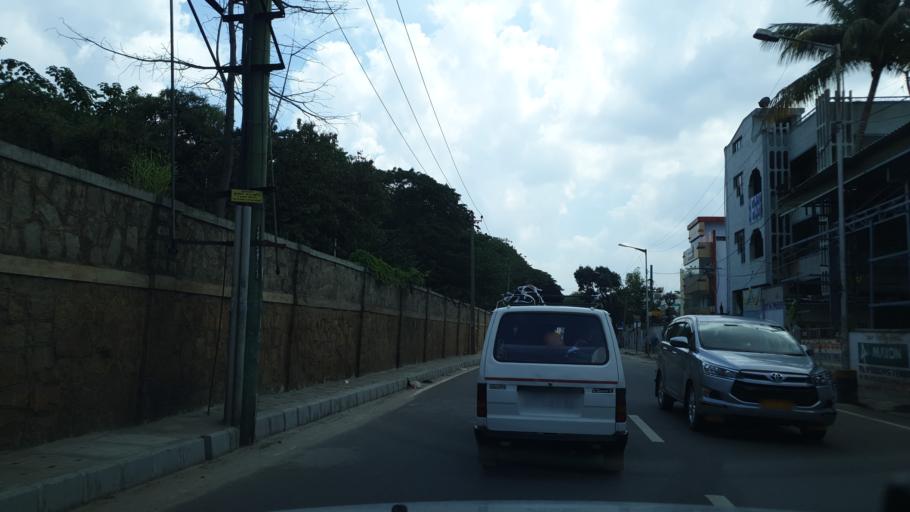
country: IN
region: Karnataka
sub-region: Bangalore Urban
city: Bangalore
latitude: 13.0232
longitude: 77.5629
